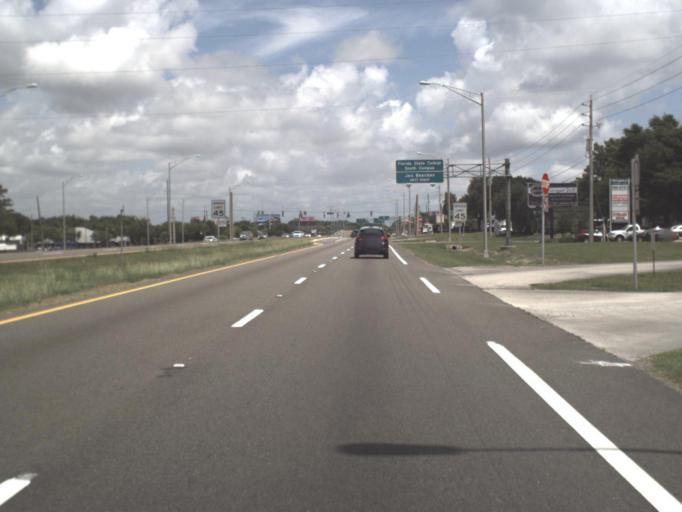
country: US
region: Florida
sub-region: Duval County
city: Jacksonville
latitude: 30.2788
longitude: -81.5590
